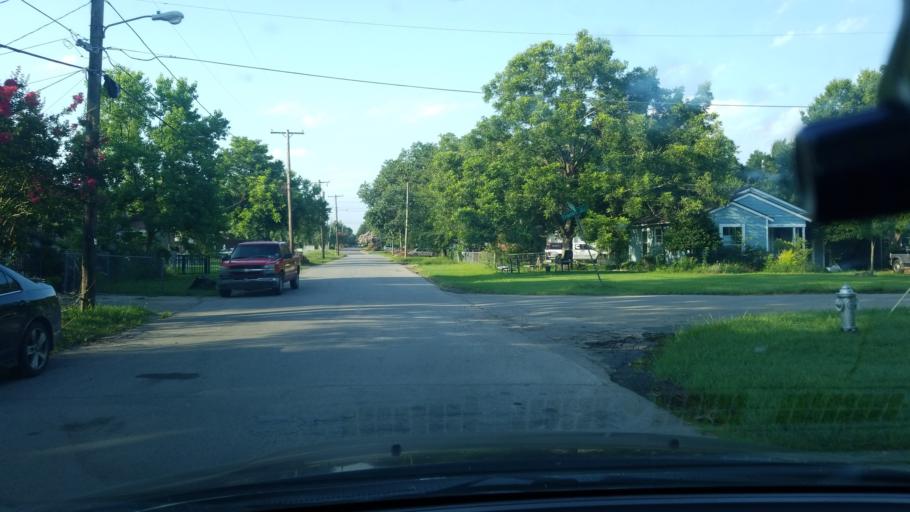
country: US
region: Texas
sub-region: Dallas County
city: Balch Springs
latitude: 32.7188
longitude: -96.6752
